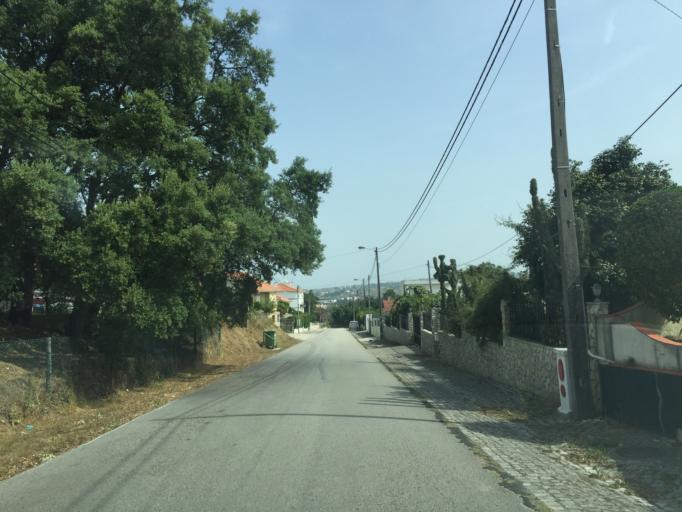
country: PT
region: Leiria
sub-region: Batalha
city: Batalha
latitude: 39.6519
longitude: -8.8369
